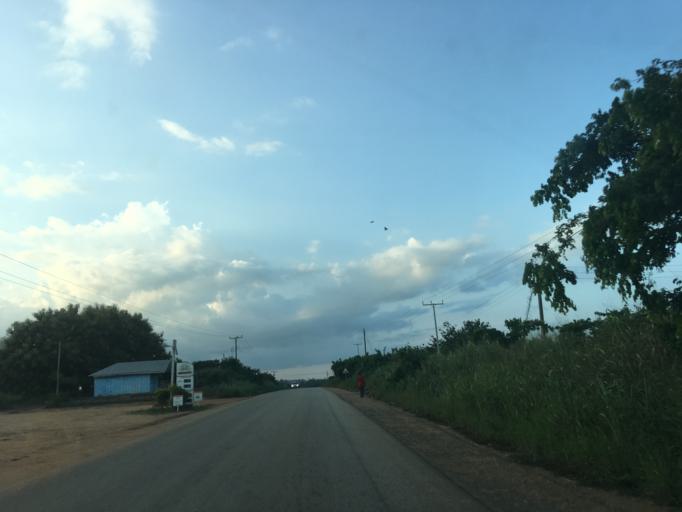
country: GH
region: Western
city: Bibiani
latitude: 6.6434
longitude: -2.4250
